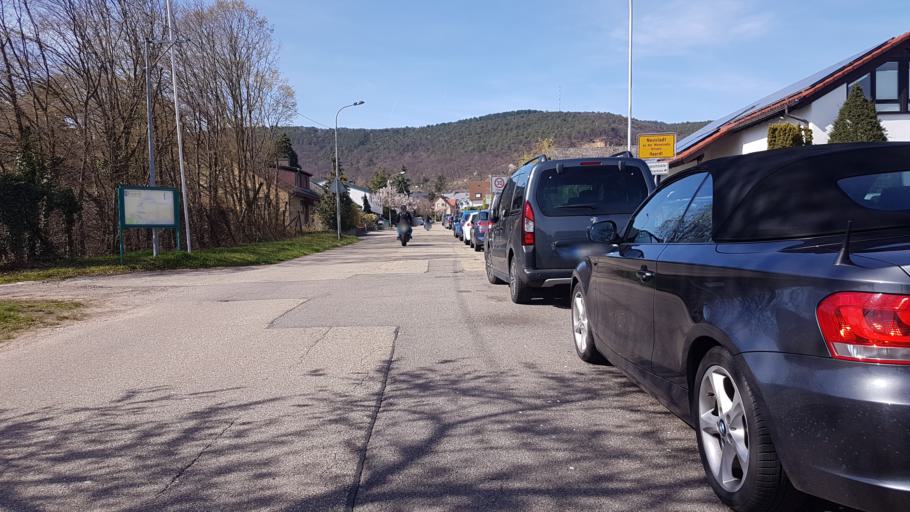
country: DE
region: Rheinland-Pfalz
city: Neustadt
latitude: 49.3670
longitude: 8.1523
